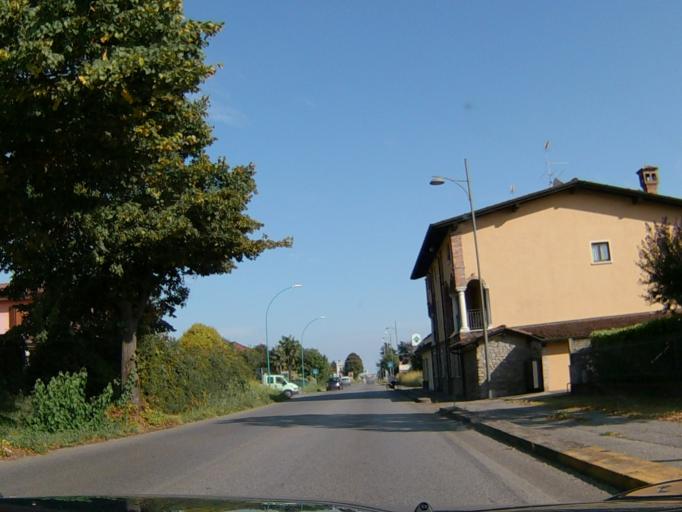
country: IT
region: Lombardy
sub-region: Provincia di Brescia
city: Cologne
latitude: 45.5772
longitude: 9.9397
